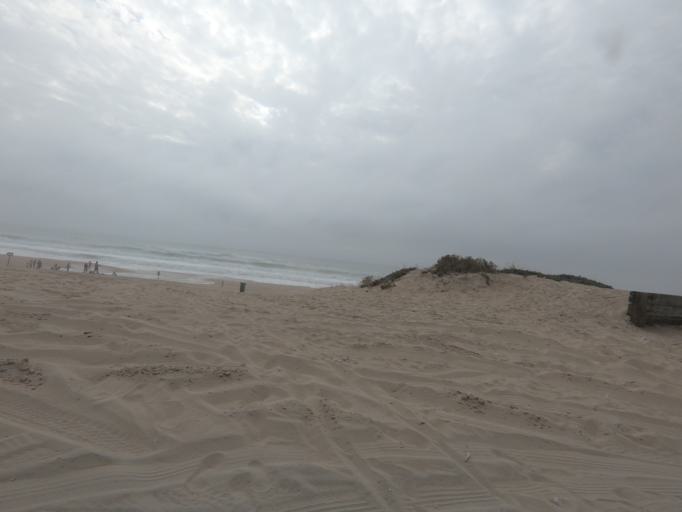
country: PT
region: Setubal
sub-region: Almada
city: Charneca
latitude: 38.5696
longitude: -9.1942
